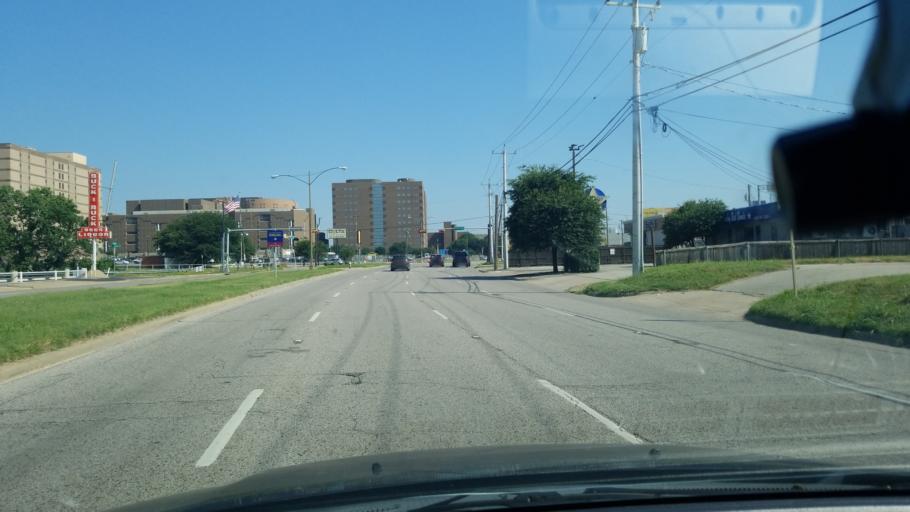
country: US
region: Texas
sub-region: Dallas County
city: Dallas
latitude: 32.7734
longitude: -96.8128
